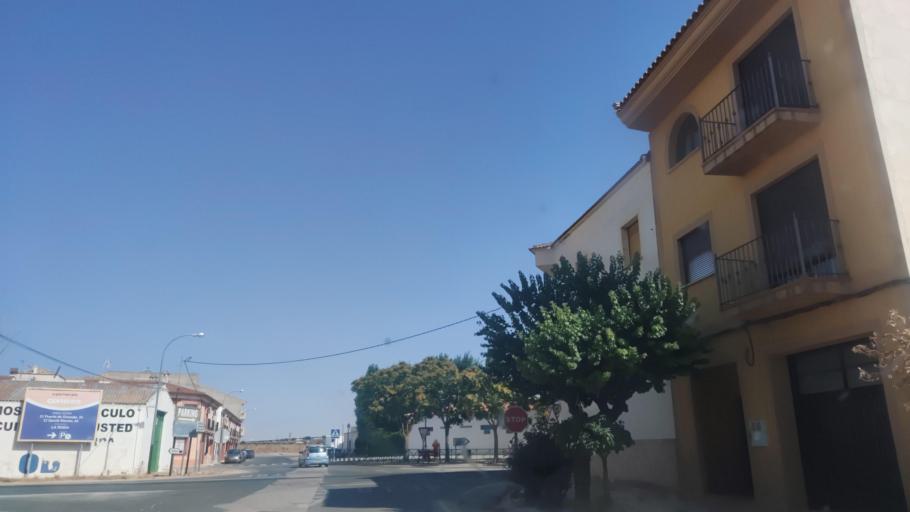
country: ES
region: Castille-La Mancha
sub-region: Provincia de Albacete
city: La Gineta
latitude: 39.1170
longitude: -2.0003
